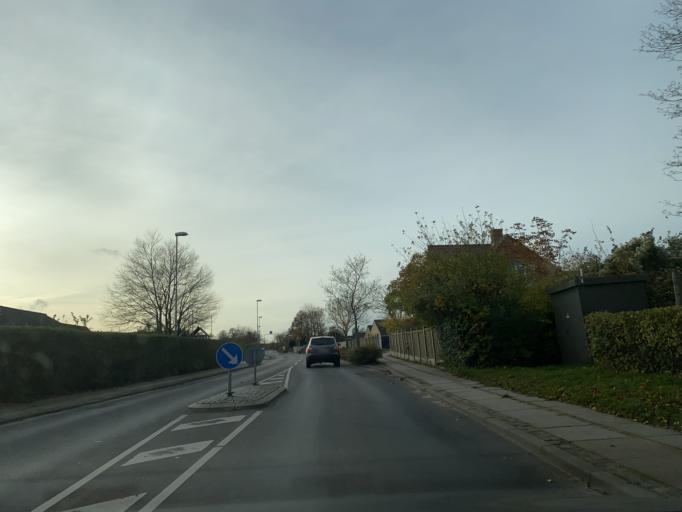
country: DK
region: Central Jutland
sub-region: Skanderborg Kommune
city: Skovby
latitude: 56.1588
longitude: 9.9505
